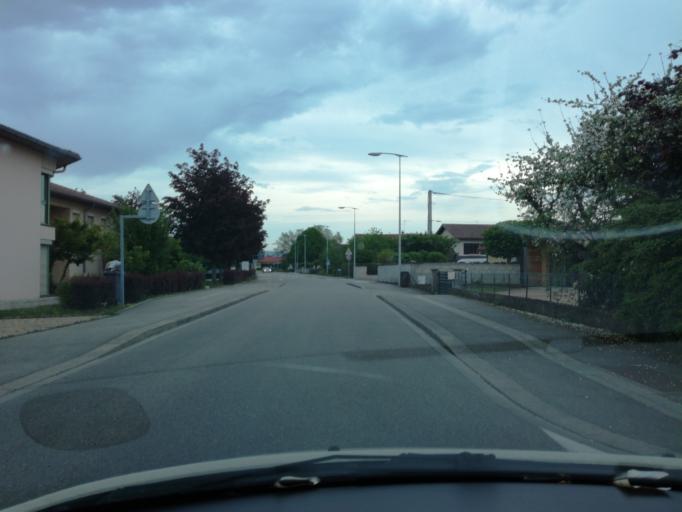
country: FR
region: Rhone-Alpes
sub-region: Departement de l'Ain
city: Peronnas
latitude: 46.1816
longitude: 5.2064
